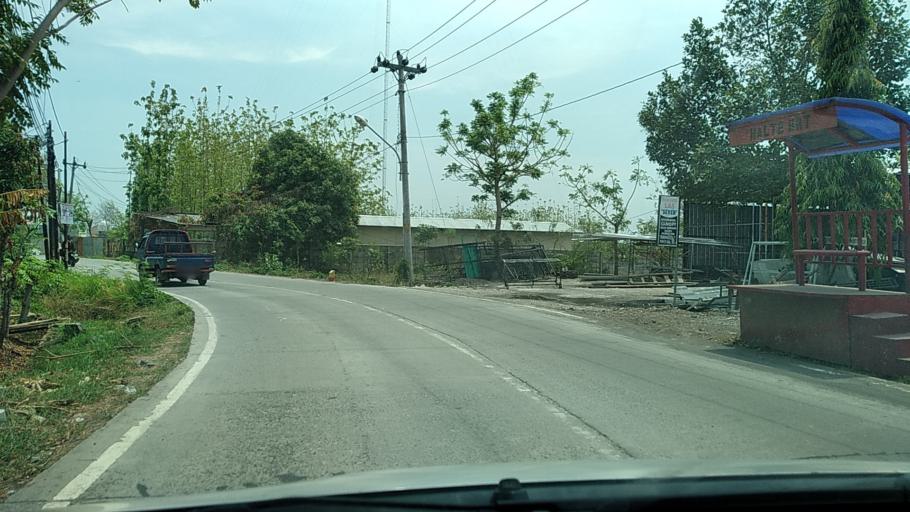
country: ID
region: Central Java
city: Mranggen
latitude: -7.0425
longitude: 110.4670
